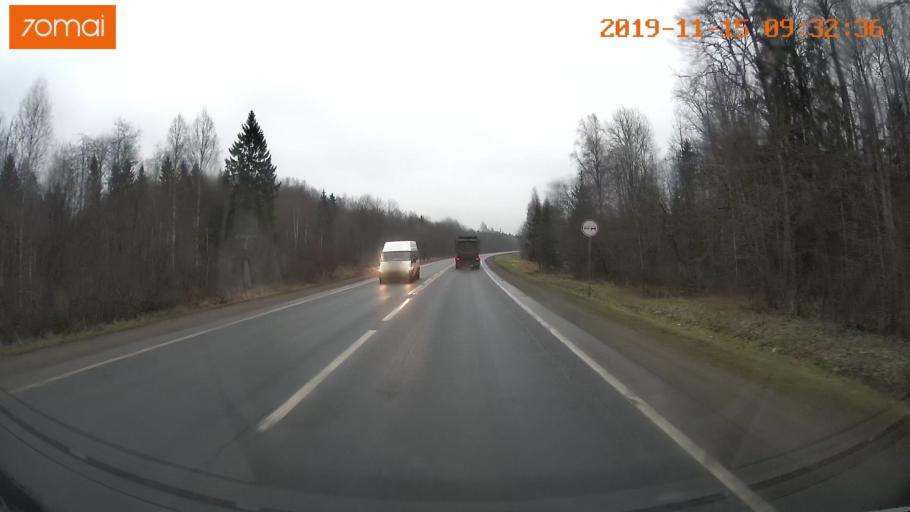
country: RU
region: Vologda
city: Sheksna
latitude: 59.2709
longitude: 38.3393
